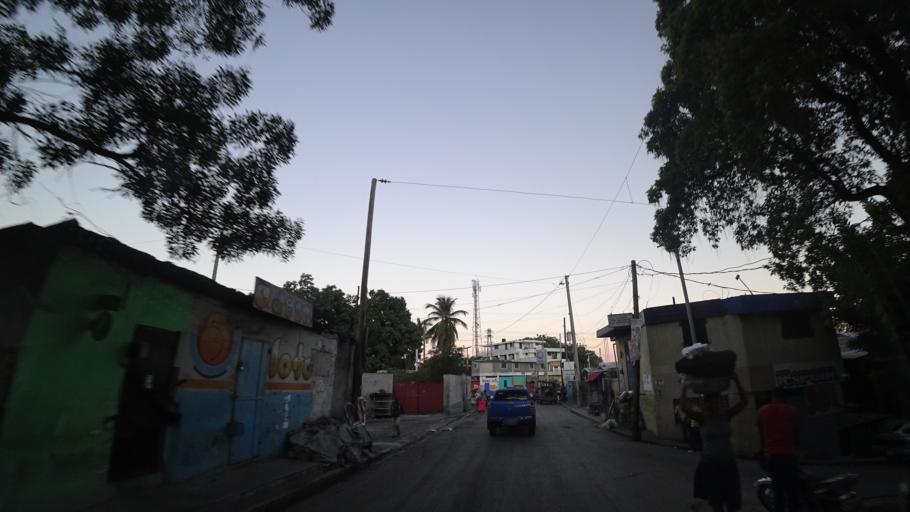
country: HT
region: Ouest
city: Delmas 73
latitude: 18.5455
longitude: -72.3168
